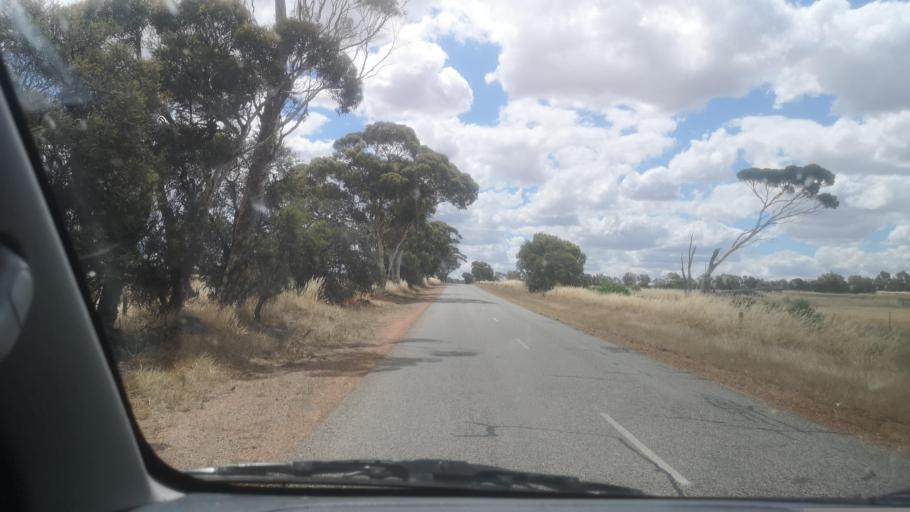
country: AU
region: Western Australia
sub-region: Beverley
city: Beverley
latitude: -31.9767
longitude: 117.0821
